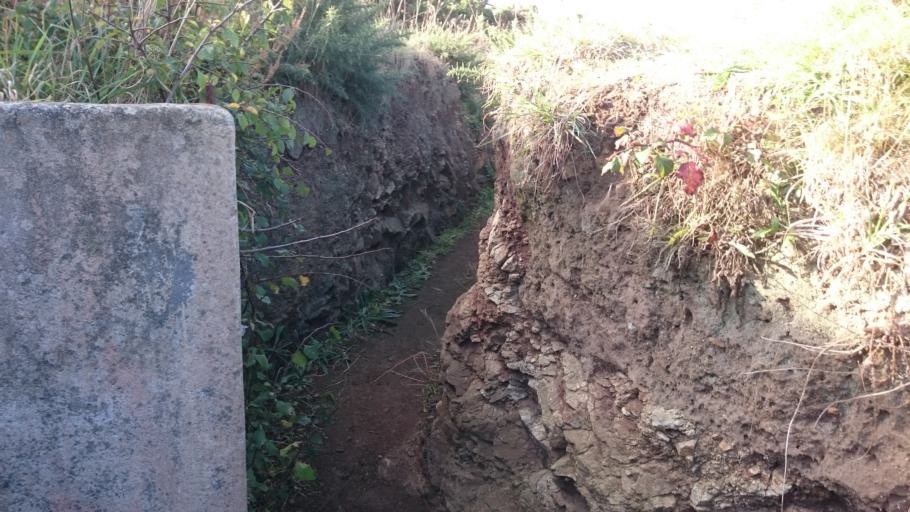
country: GG
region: St Peter Port
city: Saint Peter Port
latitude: 49.4269
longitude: -2.6673
